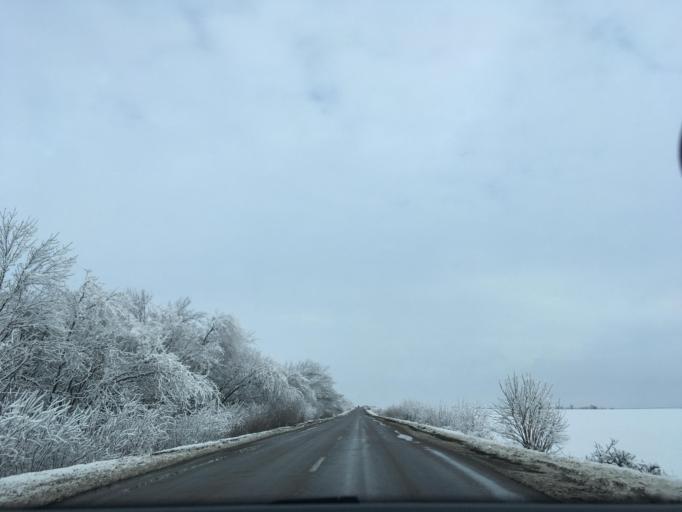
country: UA
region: Luhansk
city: Lozno-Oleksandrivka
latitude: 49.9884
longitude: 39.0148
